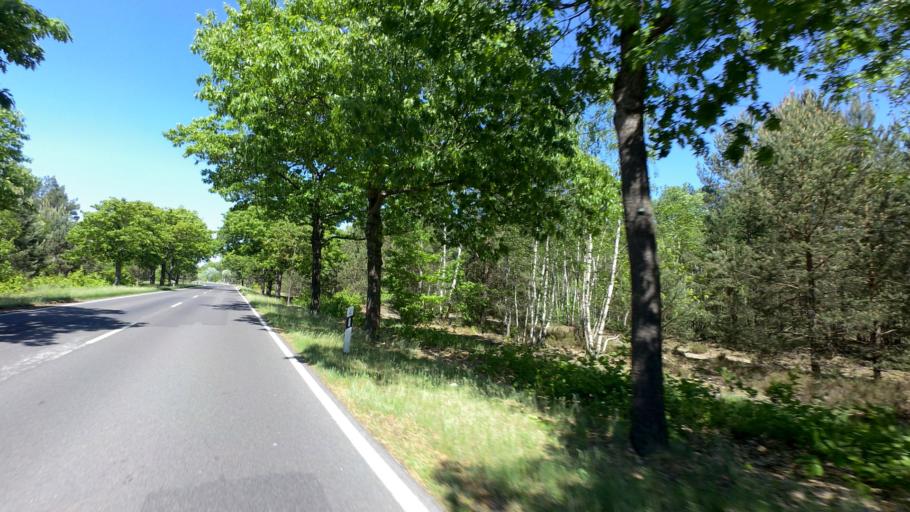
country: DE
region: Brandenburg
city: Drachhausen
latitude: 51.9325
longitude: 14.3446
